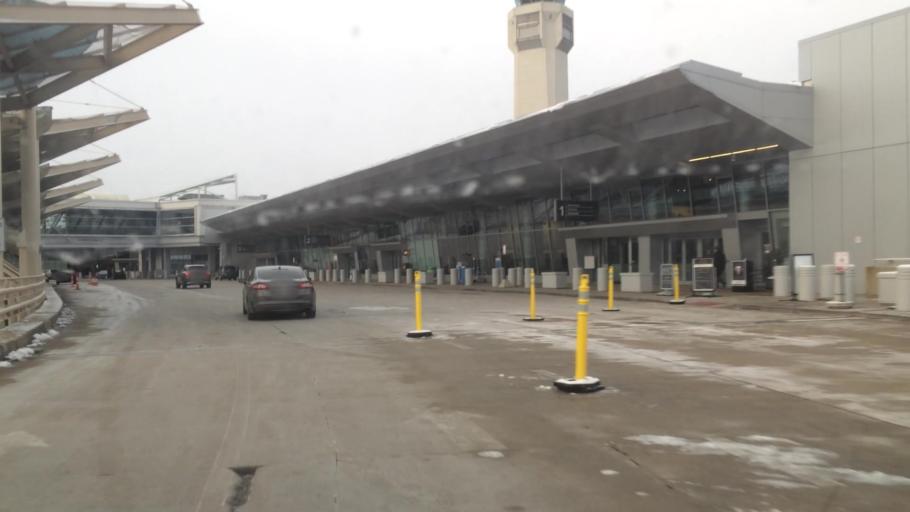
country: US
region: Ohio
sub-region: Cuyahoga County
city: Brook Park
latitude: 41.4118
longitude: -81.8369
